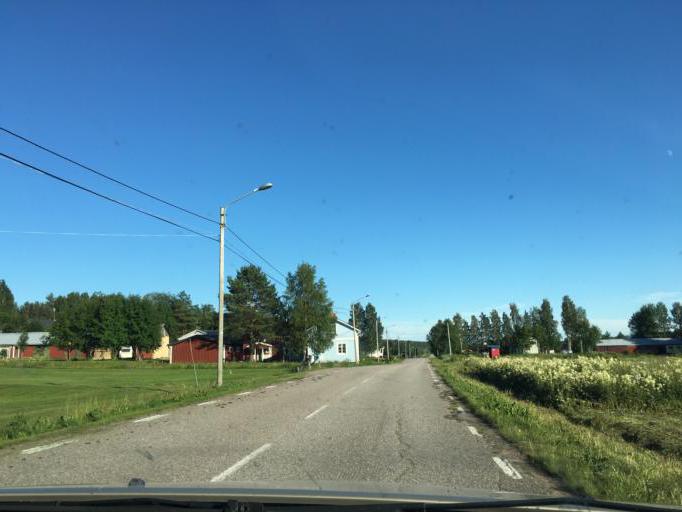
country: SE
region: Norrbotten
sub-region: Kalix Kommun
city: Rolfs
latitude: 65.9003
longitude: 22.9350
